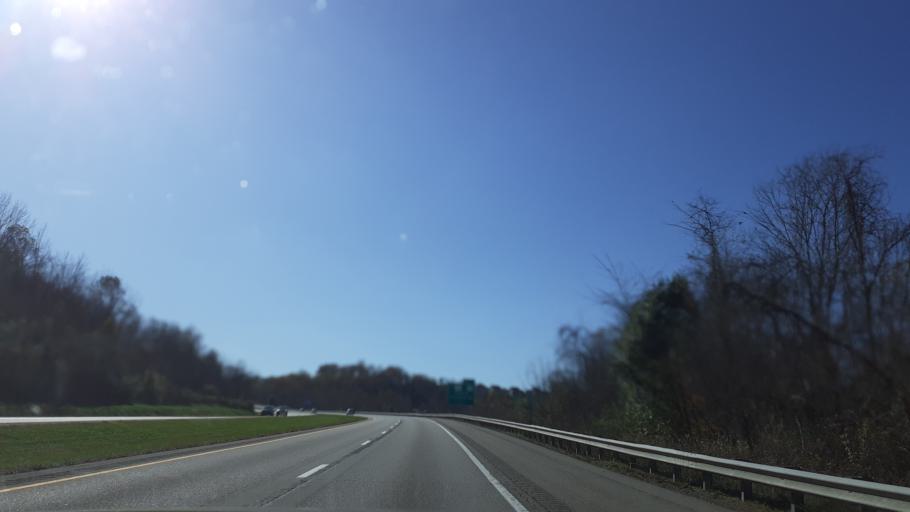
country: US
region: West Virginia
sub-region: Monongalia County
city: Cheat Lake
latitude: 39.6620
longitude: -79.8805
